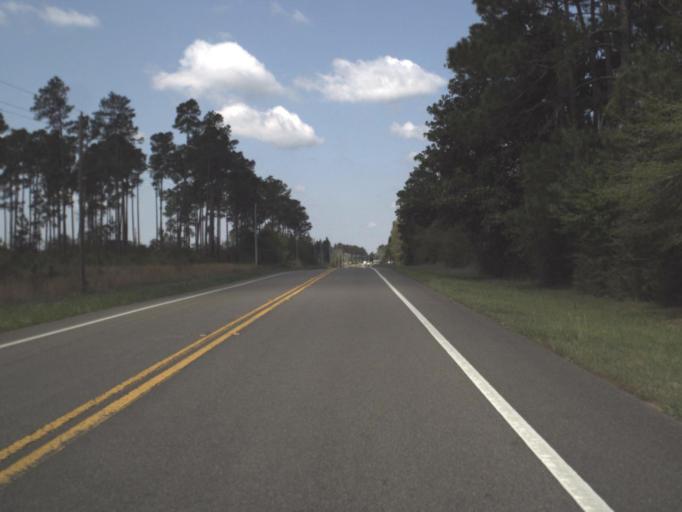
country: US
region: Florida
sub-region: Santa Rosa County
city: Point Baker
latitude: 30.8567
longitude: -86.8617
